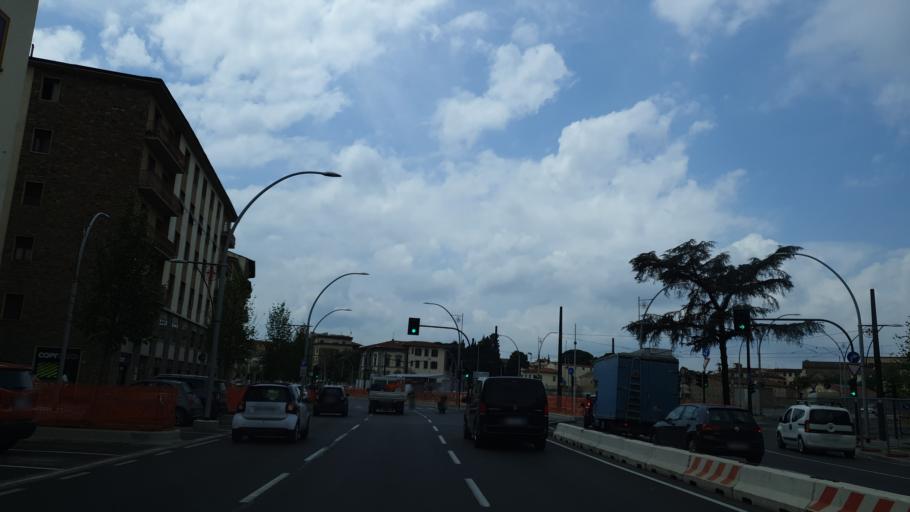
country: IT
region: Tuscany
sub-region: Province of Florence
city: Florence
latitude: 43.7825
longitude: 11.2438
